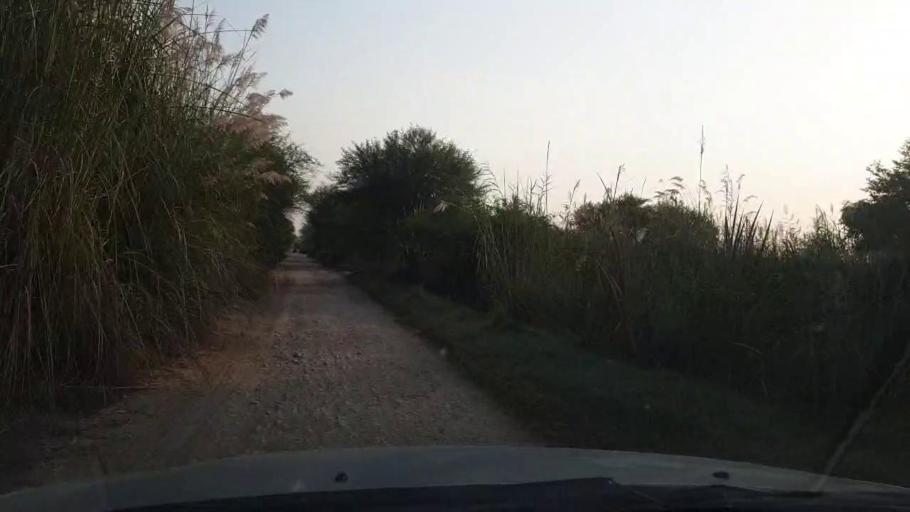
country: PK
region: Sindh
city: Tando Muhammad Khan
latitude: 25.0058
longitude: 68.4355
